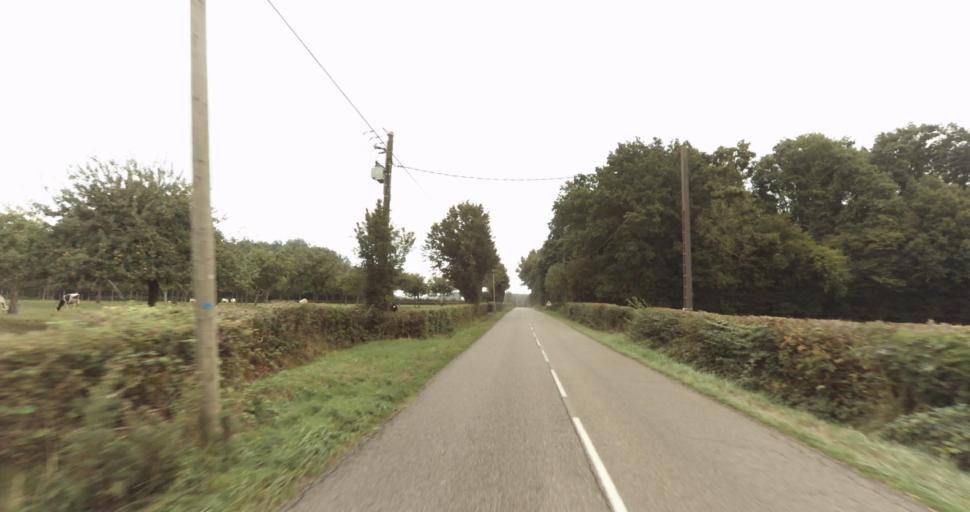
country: FR
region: Lower Normandy
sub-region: Departement de l'Orne
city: Vimoutiers
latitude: 48.8876
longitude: 0.1959
